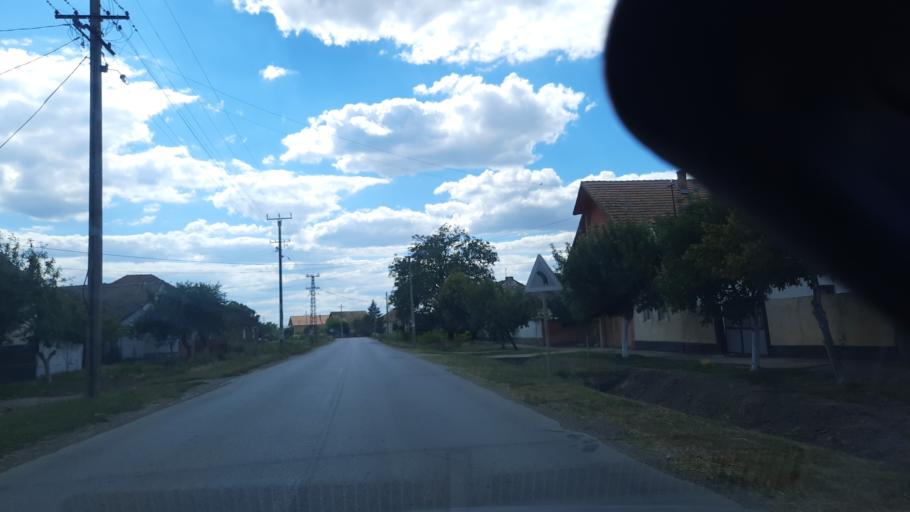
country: RS
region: Autonomna Pokrajina Vojvodina
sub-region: Sremski Okrug
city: Pecinci
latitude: 44.9264
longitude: 19.9971
